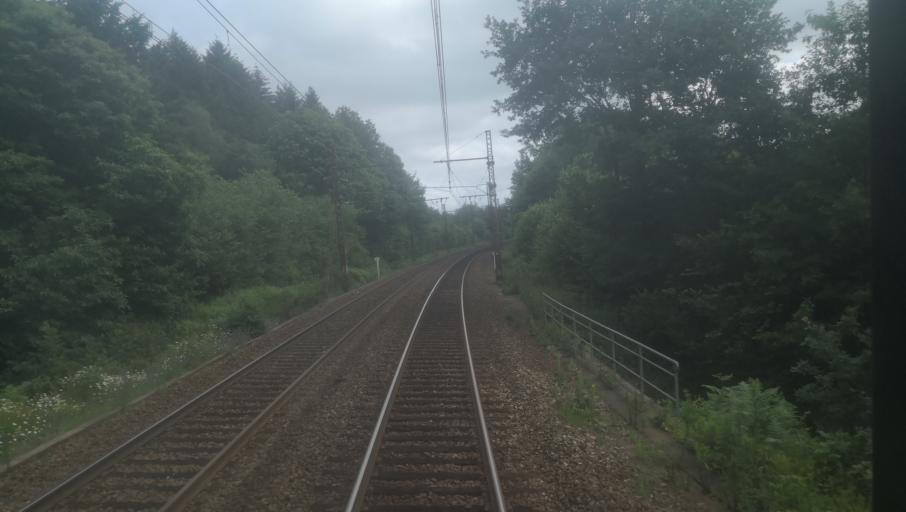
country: FR
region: Limousin
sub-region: Departement de la Haute-Vienne
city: Le Palais-sur-Vienne
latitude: 45.8734
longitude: 1.3198
